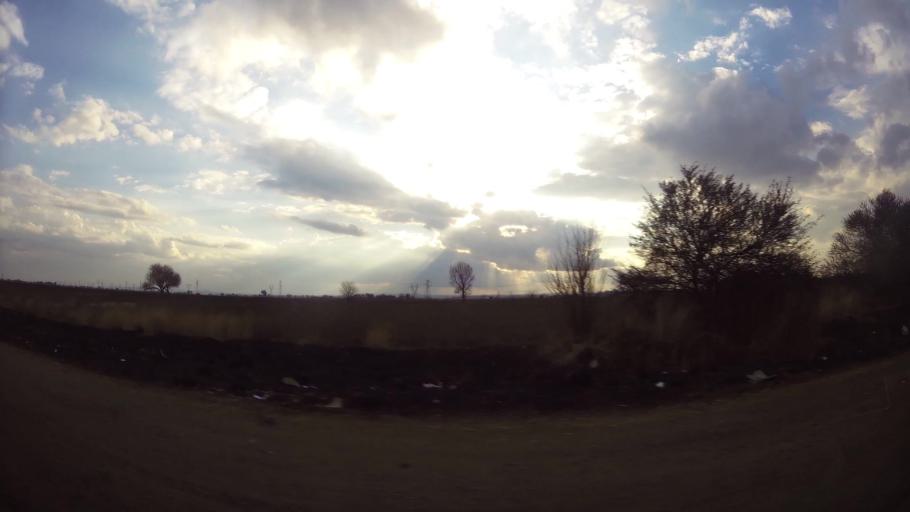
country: ZA
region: Gauteng
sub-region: Sedibeng District Municipality
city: Vanderbijlpark
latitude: -26.6661
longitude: 27.7961
